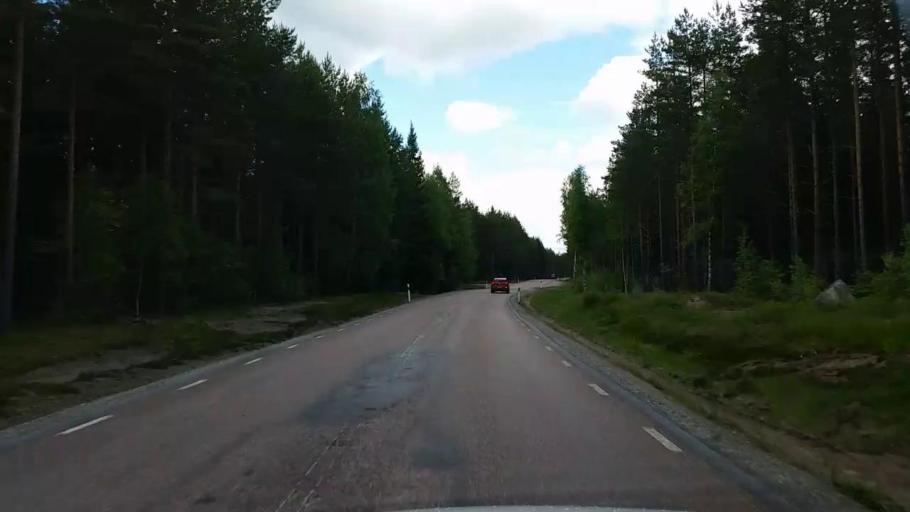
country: SE
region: Vaestmanland
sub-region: Fagersta Kommun
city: Fagersta
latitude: 59.8971
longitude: 15.8205
